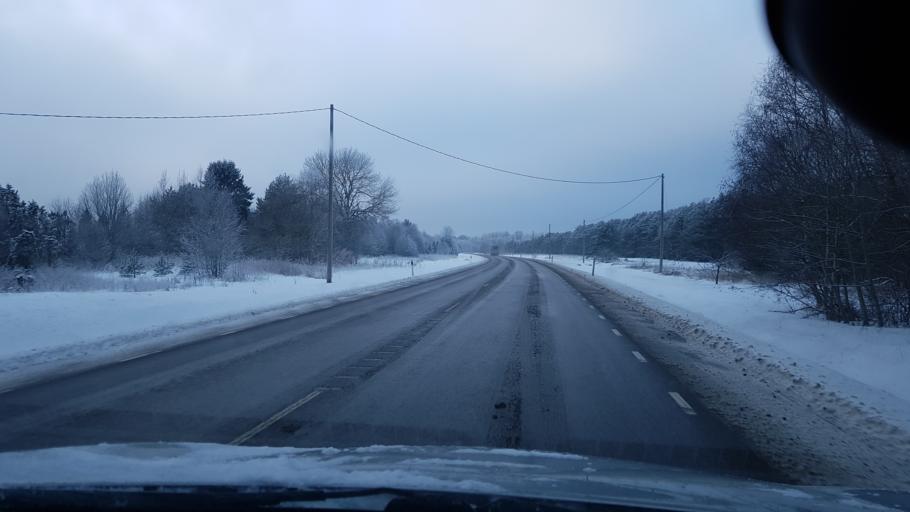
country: EE
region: Harju
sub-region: Paldiski linn
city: Paldiski
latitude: 59.3390
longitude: 24.2160
